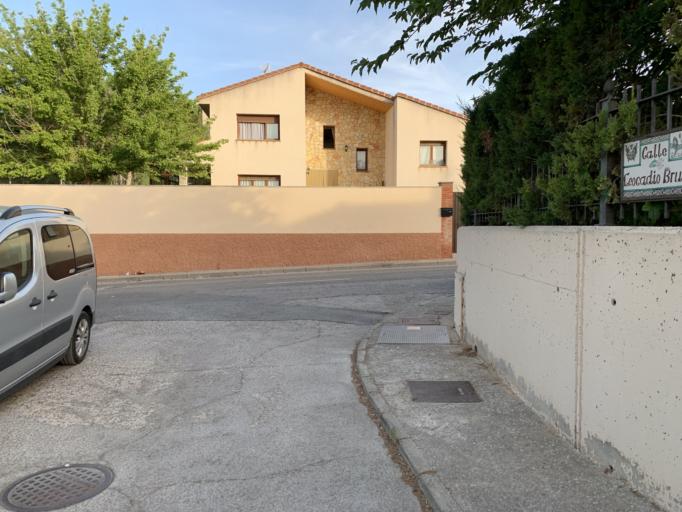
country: ES
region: Aragon
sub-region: Provincia de Teruel
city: Teruel
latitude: 40.3530
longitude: -1.1161
